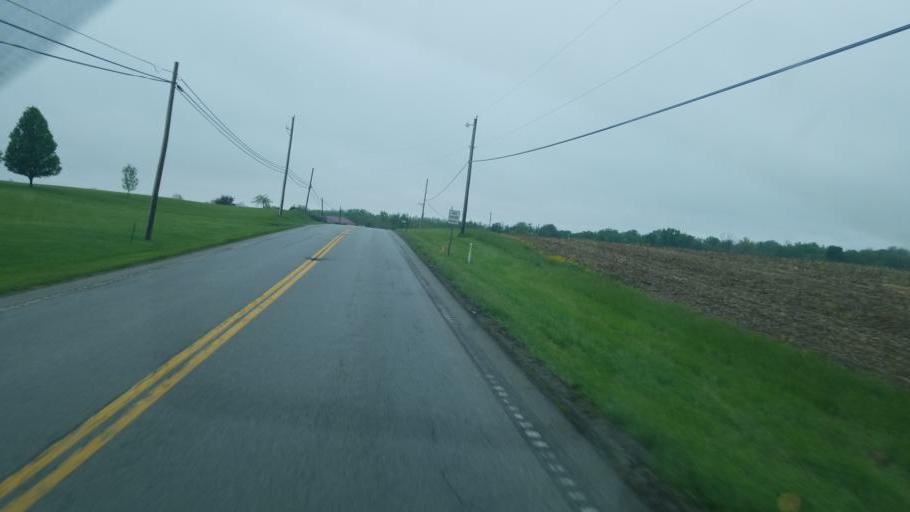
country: US
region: Ohio
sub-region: Highland County
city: Hillsboro
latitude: 39.2783
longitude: -83.5939
